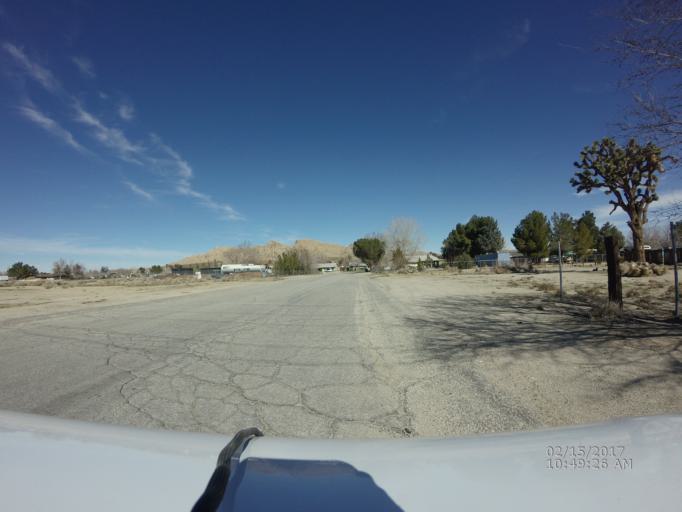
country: US
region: California
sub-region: Los Angeles County
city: Lake Los Angeles
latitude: 34.5801
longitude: -117.8488
